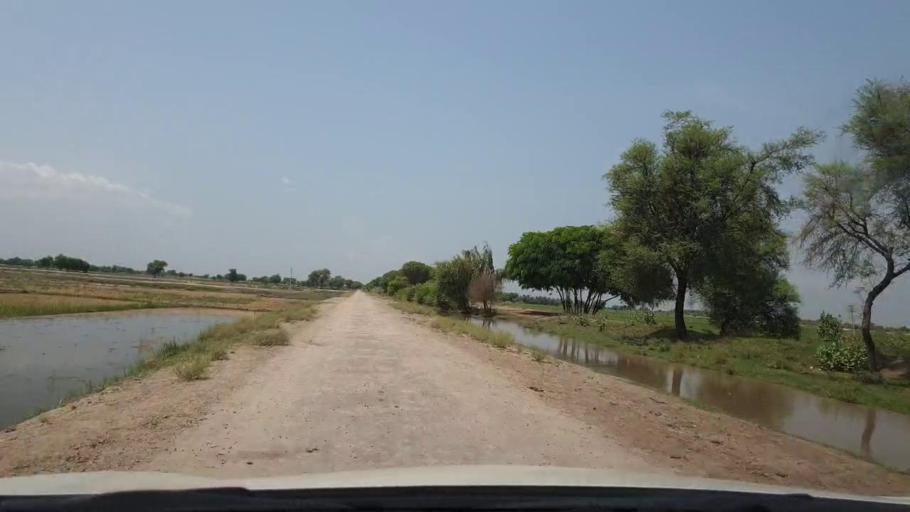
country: PK
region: Sindh
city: Ratodero
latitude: 27.8114
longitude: 68.2465
